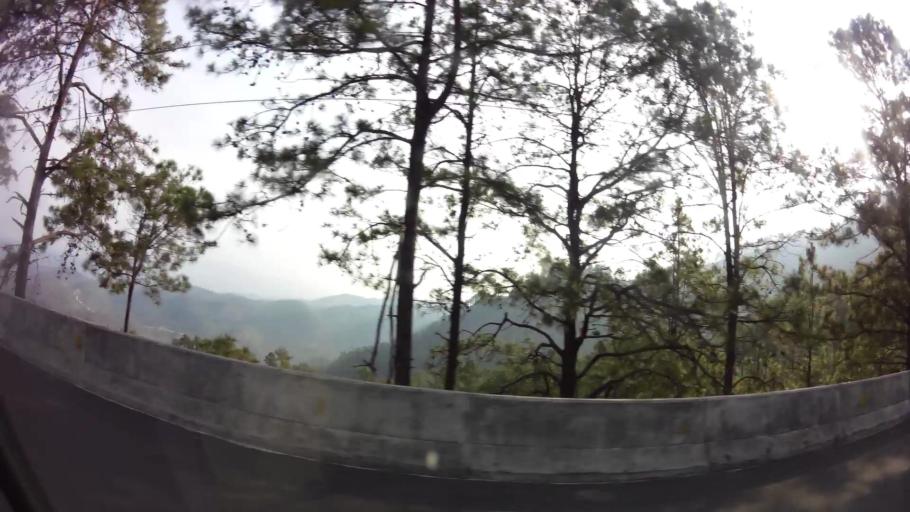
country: HN
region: Comayagua
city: Flores
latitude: 14.2848
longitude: -87.4957
